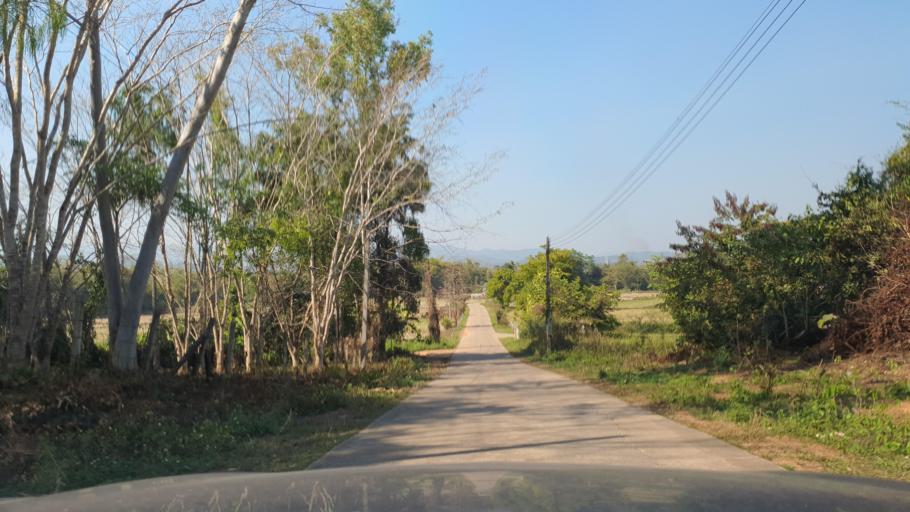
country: TH
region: Chiang Rai
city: Mae Lao
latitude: 19.7952
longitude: 99.7029
